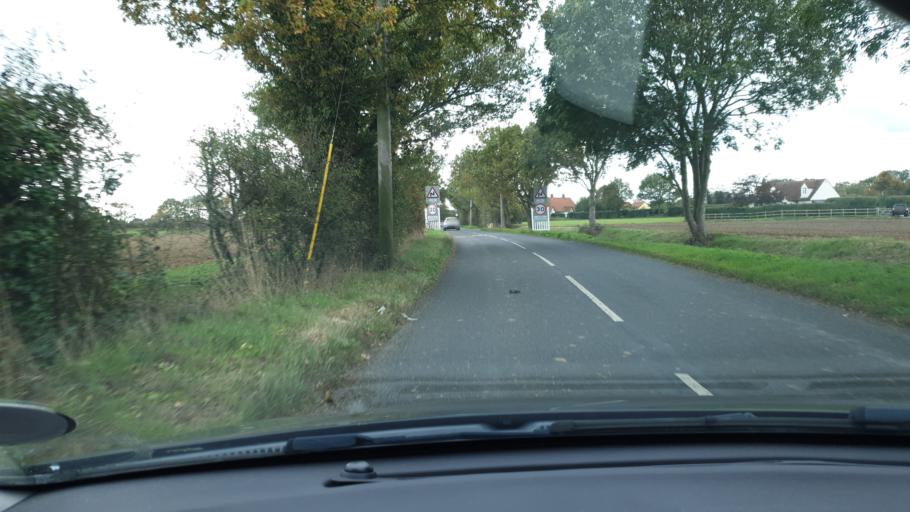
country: GB
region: England
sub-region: Essex
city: Manningtree
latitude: 51.9223
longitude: 1.0476
